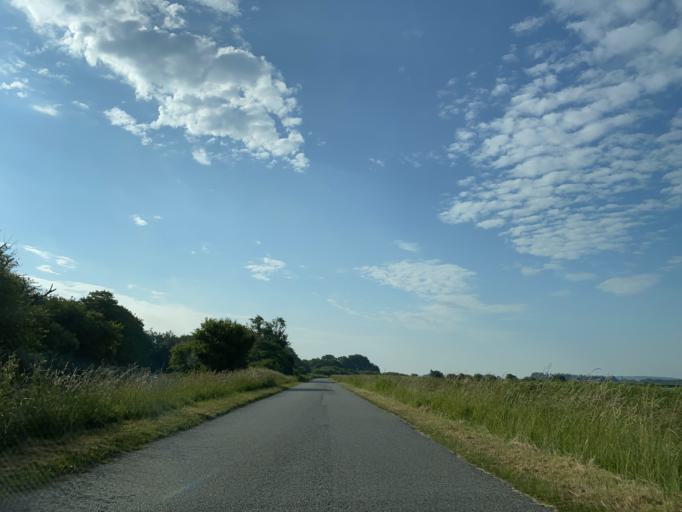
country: DK
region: South Denmark
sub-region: Haderslev Kommune
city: Haderslev
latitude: 55.1708
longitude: 9.4874
